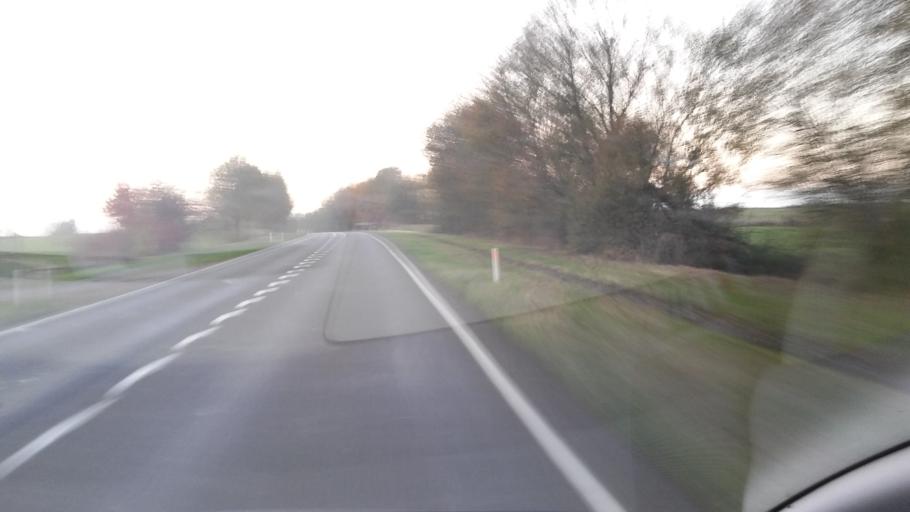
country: BE
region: Wallonia
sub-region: Province du Luxembourg
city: Etalle
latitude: 49.6756
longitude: 5.6219
